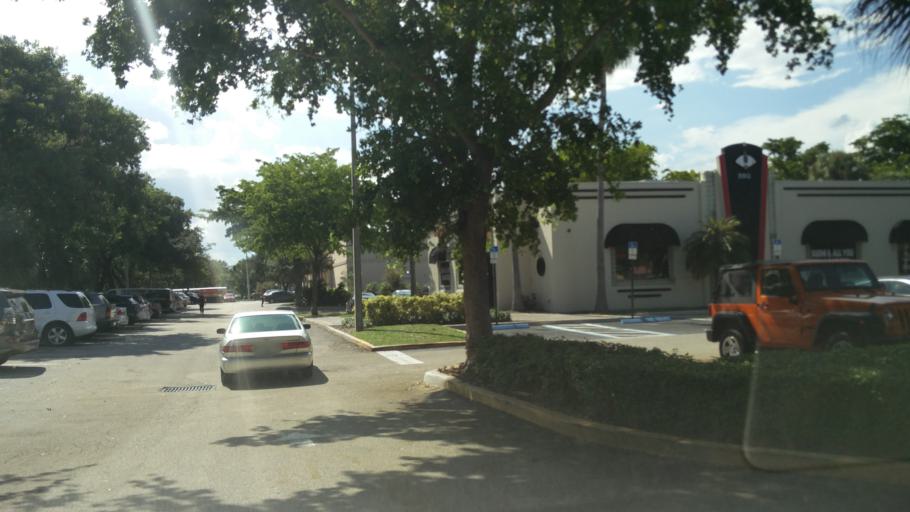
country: US
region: Florida
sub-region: Broward County
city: Plantation
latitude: 26.1657
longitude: -80.2431
